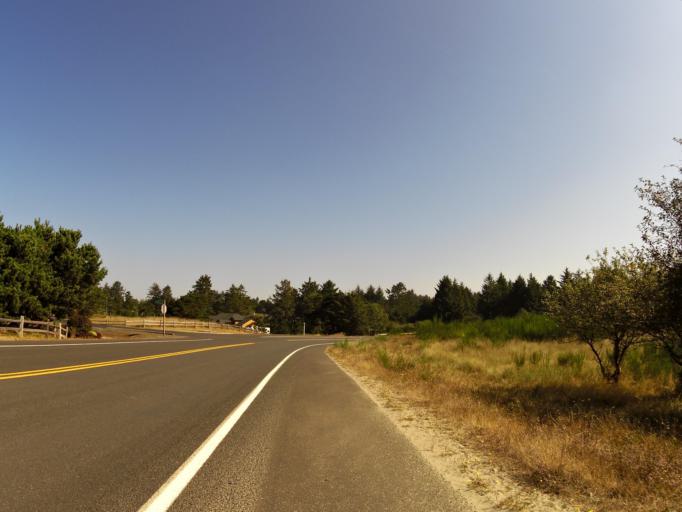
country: US
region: Oregon
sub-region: Clatsop County
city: Gearhart
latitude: 46.0491
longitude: -123.9220
